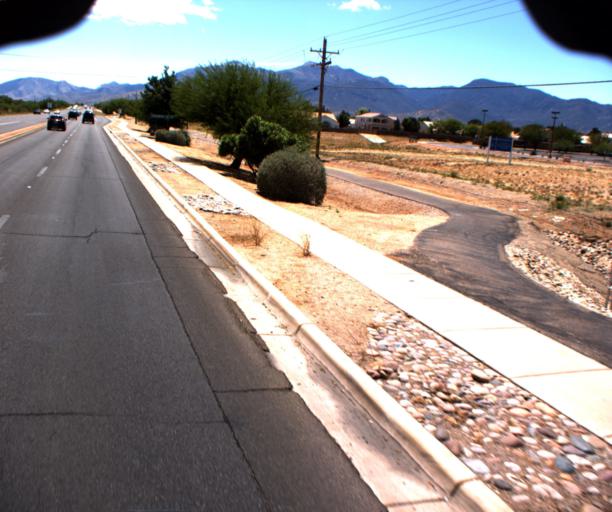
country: US
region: Arizona
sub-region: Cochise County
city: Sierra Vista
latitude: 31.5283
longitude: -110.2574
